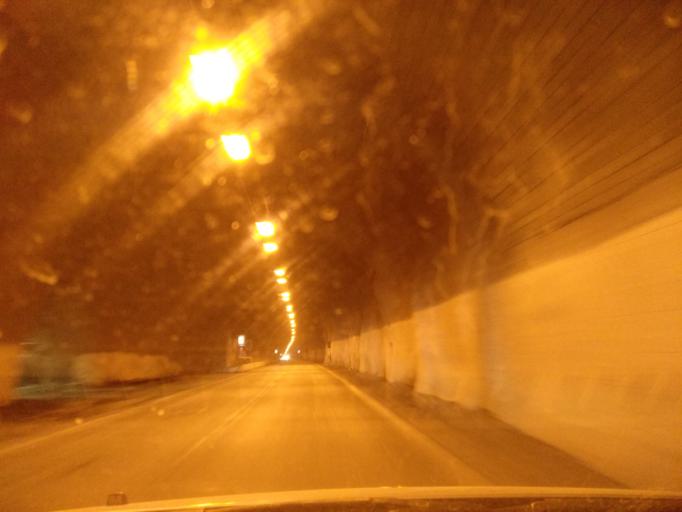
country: NO
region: Aust-Agder
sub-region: Bykle
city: Hovden
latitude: 59.8485
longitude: 7.0839
